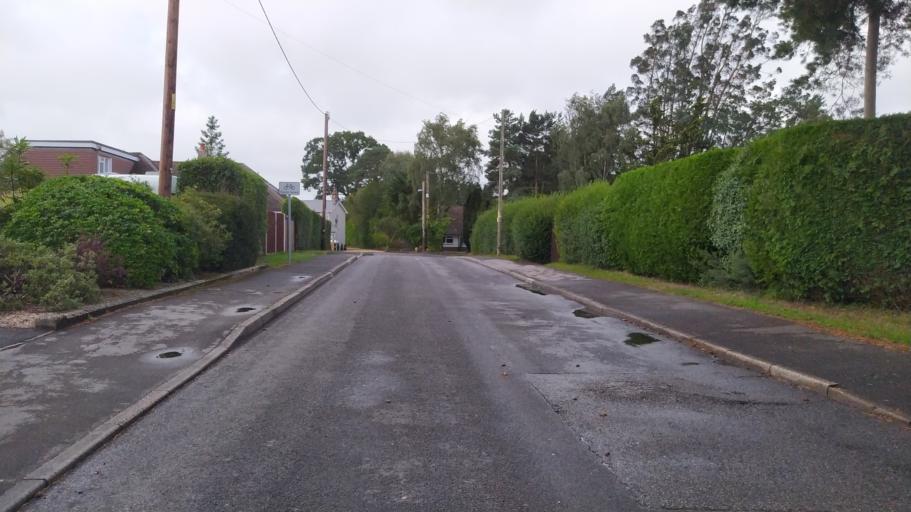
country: GB
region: England
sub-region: Dorset
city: St Leonards
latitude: 50.8337
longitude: -1.8369
